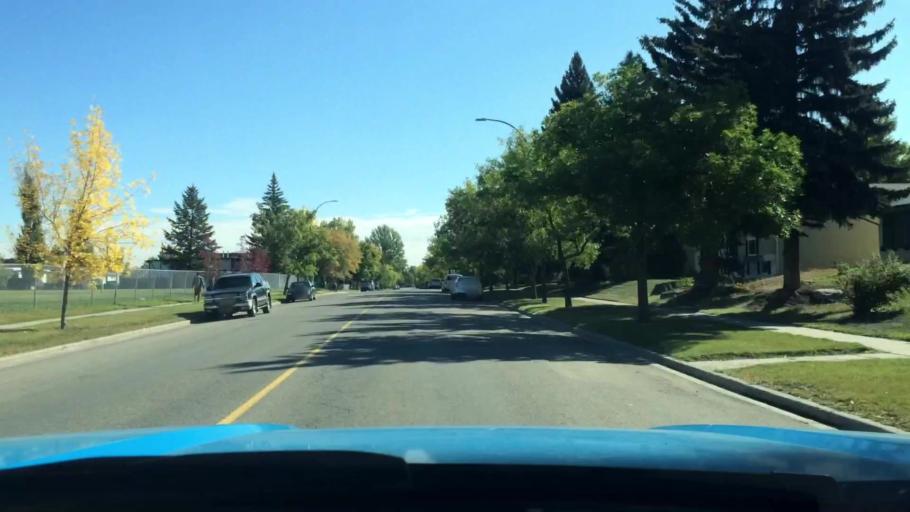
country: CA
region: Alberta
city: Calgary
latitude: 51.1178
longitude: -114.0616
